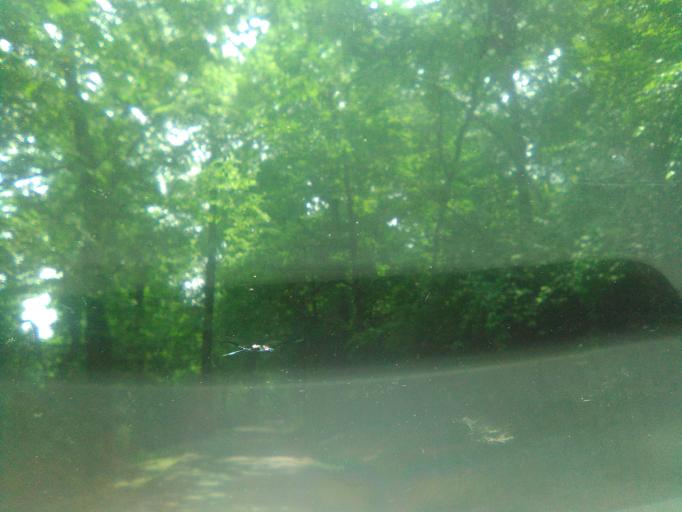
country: US
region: Tennessee
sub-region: Davidson County
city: Belle Meade
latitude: 36.0793
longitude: -86.8697
